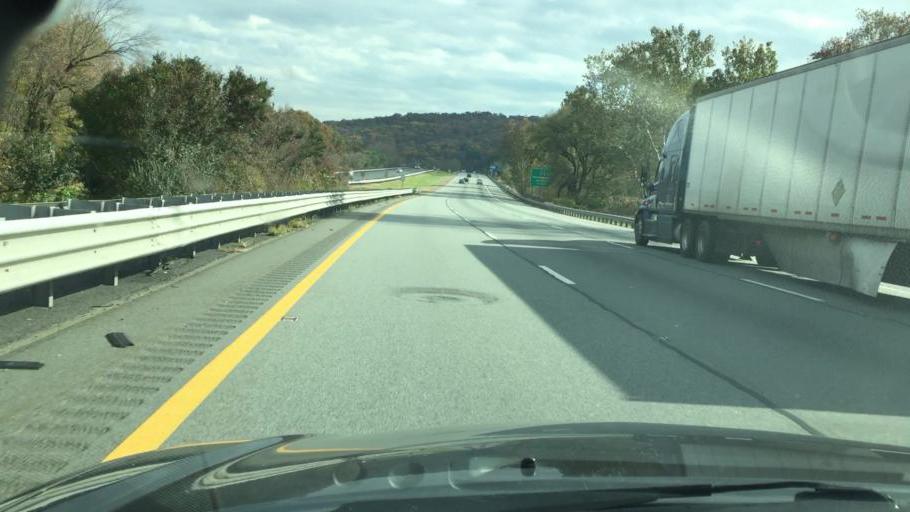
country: US
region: New Jersey
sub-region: Warren County
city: Hackettstown
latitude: 40.9212
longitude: -74.8519
